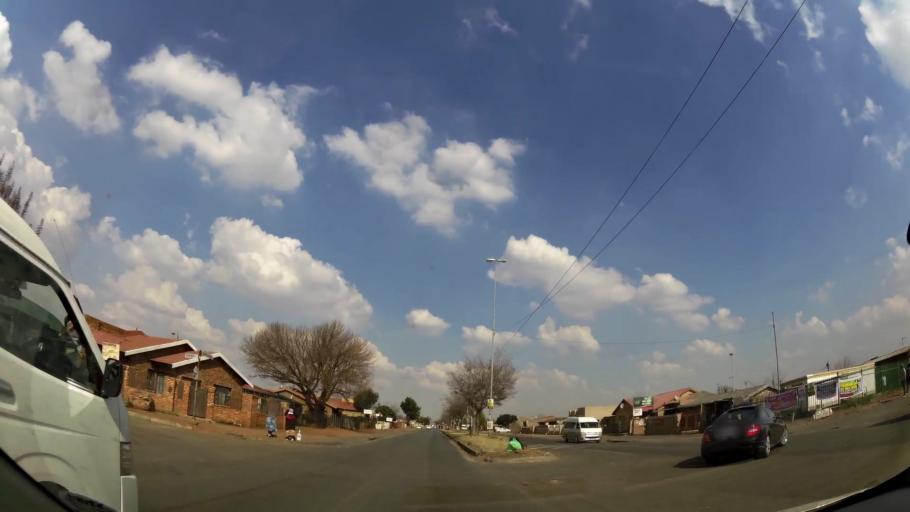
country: ZA
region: Gauteng
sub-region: Ekurhuleni Metropolitan Municipality
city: Germiston
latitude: -26.3385
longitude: 28.1618
